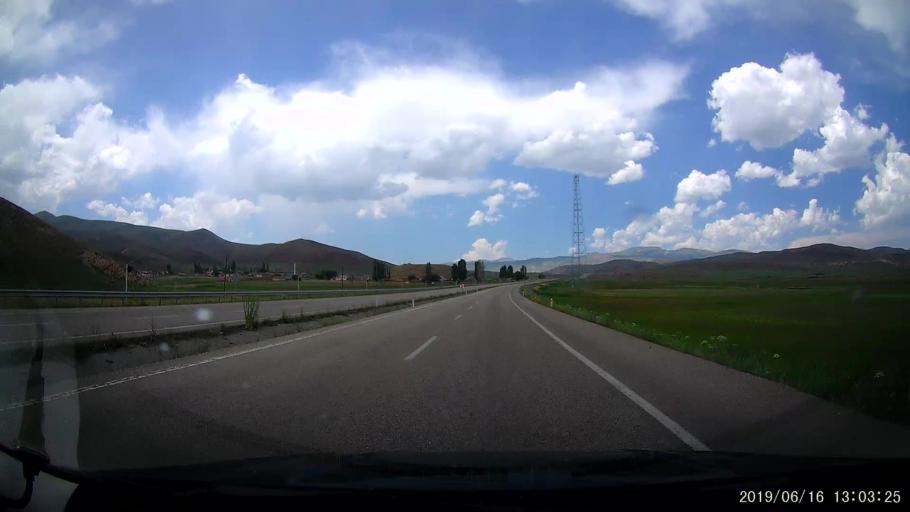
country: TR
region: Agri
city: Sulucem
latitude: 39.5811
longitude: 43.7909
